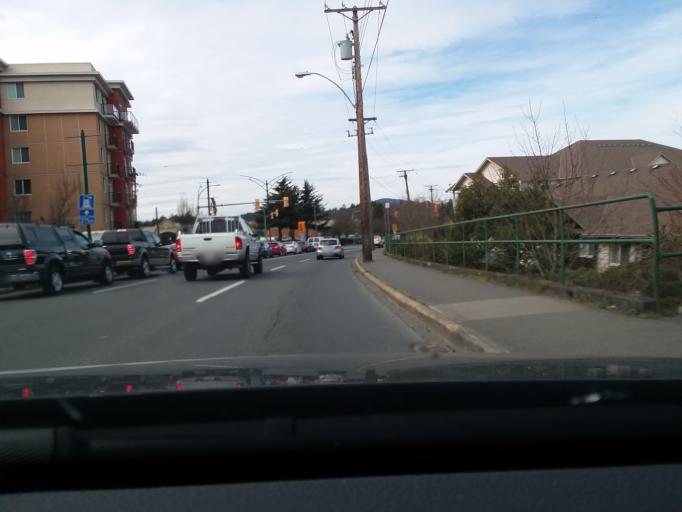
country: CA
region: British Columbia
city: Victoria
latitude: 48.4535
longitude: -123.3923
